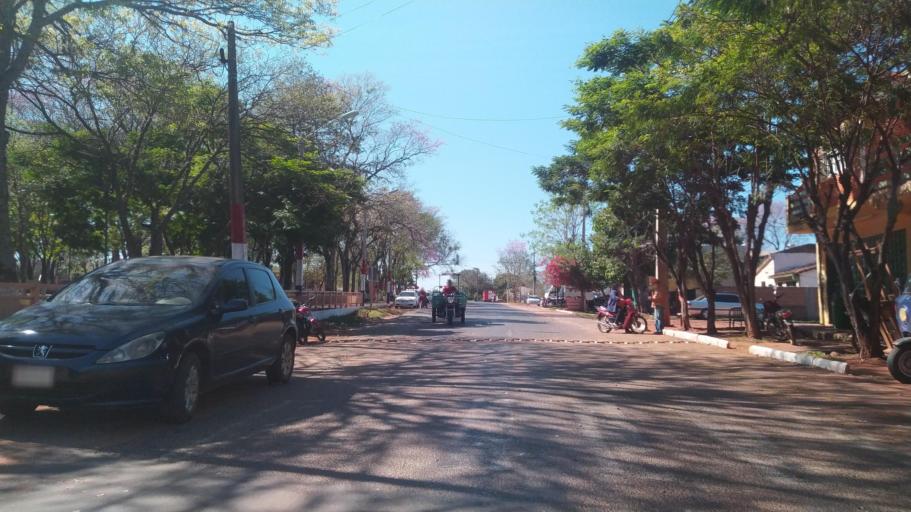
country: PY
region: Misiones
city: San Juan Bautista
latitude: -26.6709
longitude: -57.1357
